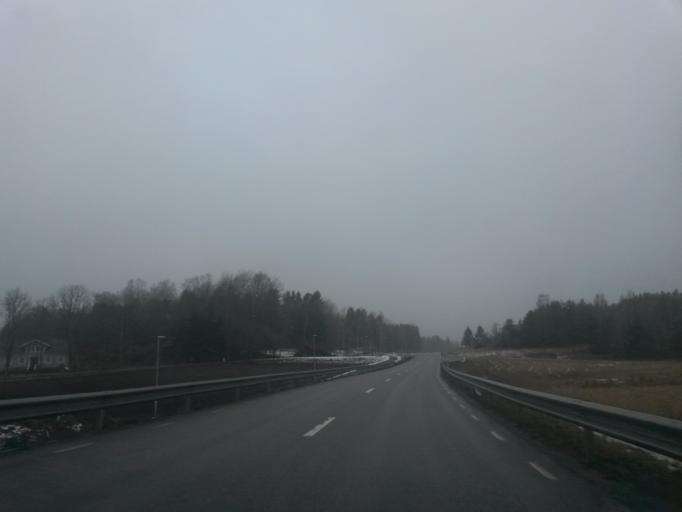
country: SE
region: Vaestra Goetaland
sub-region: Alingsas Kommun
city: Sollebrunn
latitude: 58.1087
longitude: 12.5836
